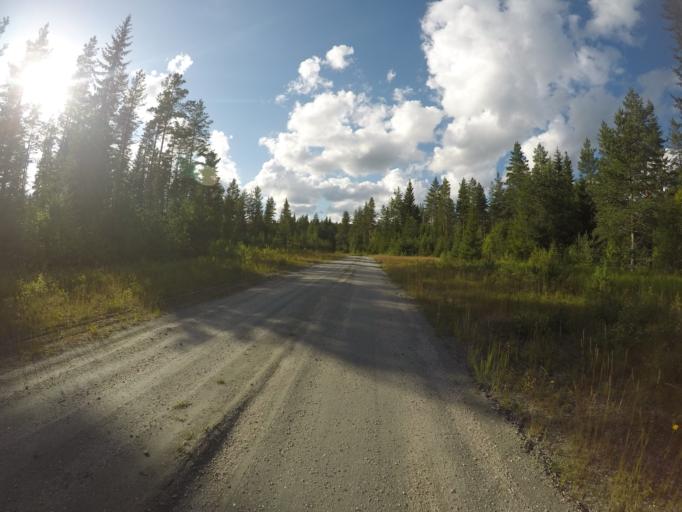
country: SE
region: OErebro
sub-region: Hallefors Kommun
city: Haellefors
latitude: 59.9852
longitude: 14.5411
